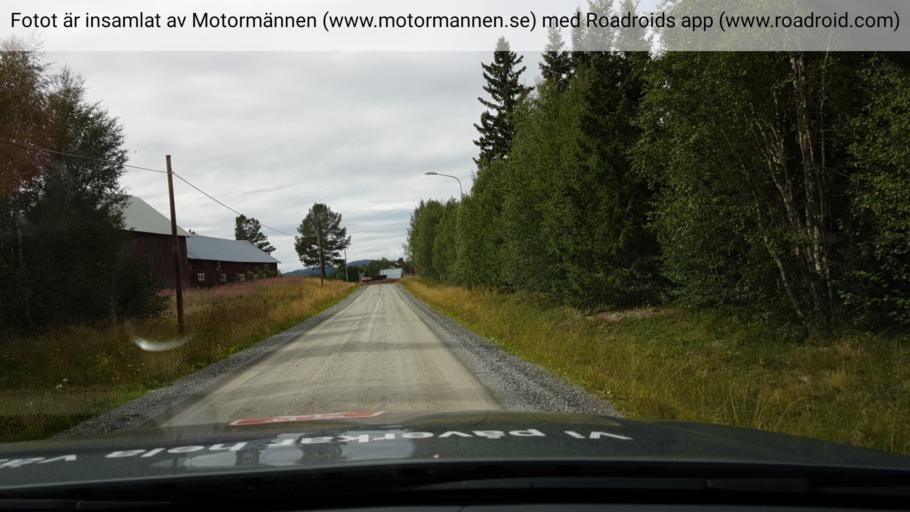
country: SE
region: Jaemtland
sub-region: Krokoms Kommun
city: Valla
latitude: 63.6980
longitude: 13.6153
